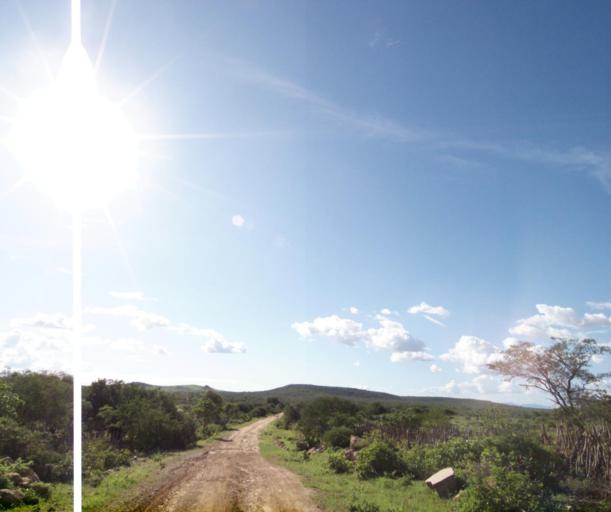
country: BR
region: Bahia
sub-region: Tanhacu
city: Tanhacu
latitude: -14.1877
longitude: -40.9450
